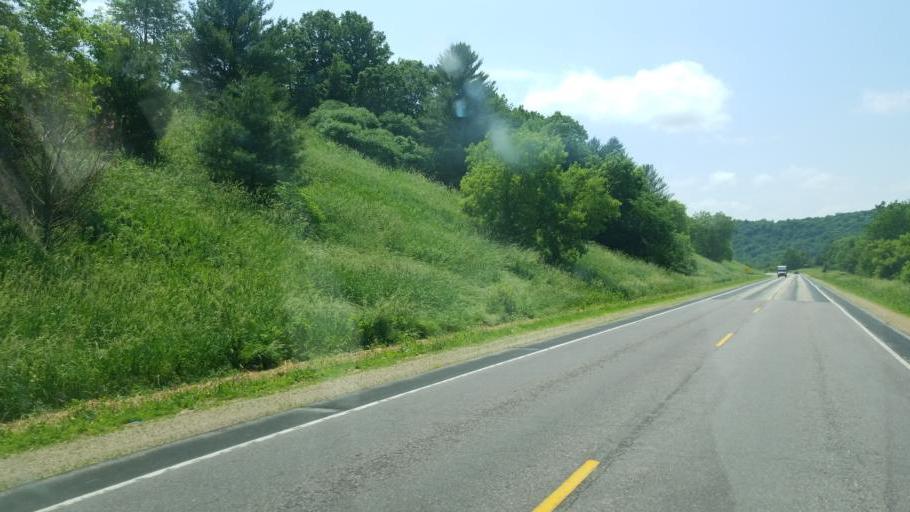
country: US
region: Wisconsin
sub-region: Monroe County
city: Cashton
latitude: 43.5867
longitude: -90.6314
